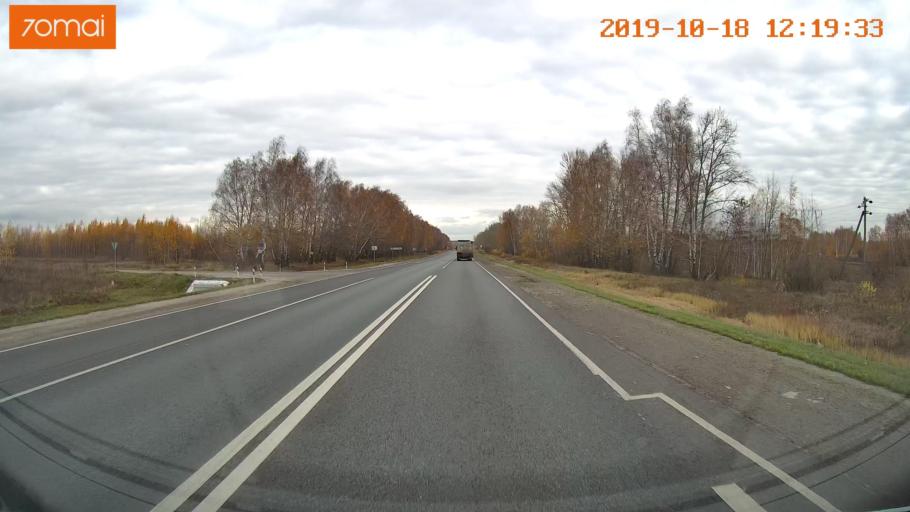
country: RU
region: Rjazan
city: Zakharovo
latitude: 54.4841
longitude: 39.4695
